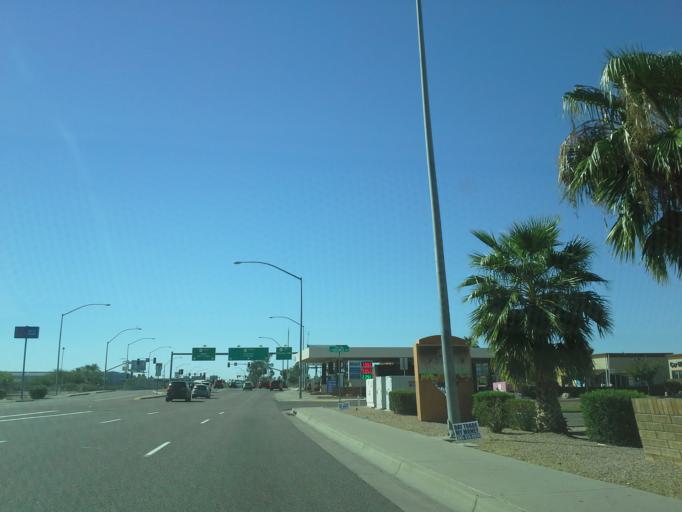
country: US
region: Arizona
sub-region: Maricopa County
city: Mesa
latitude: 33.3883
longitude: -111.8402
